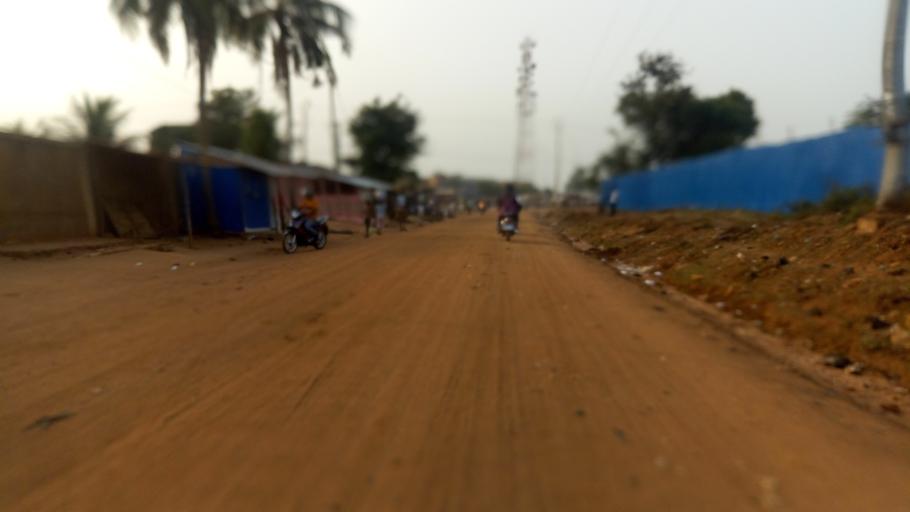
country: TG
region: Maritime
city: Tsevie
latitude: 6.3186
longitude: 1.2187
